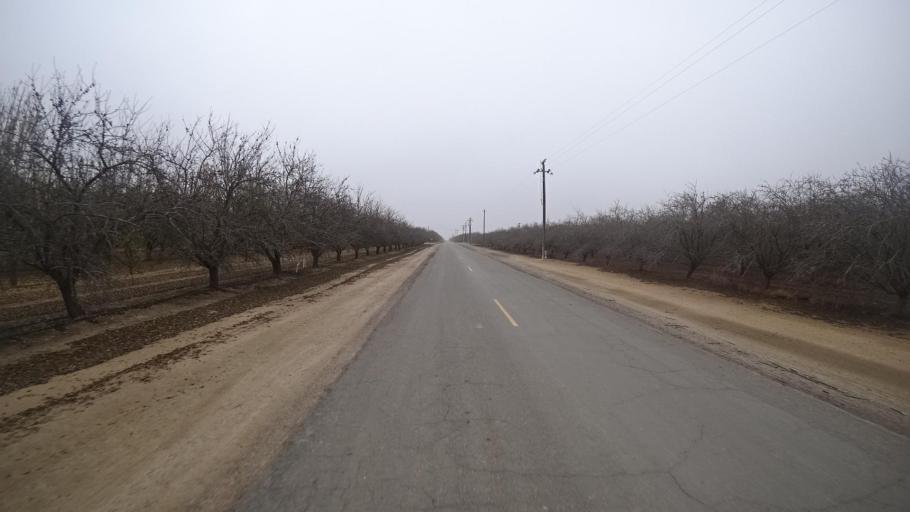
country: US
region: California
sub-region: Kern County
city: Wasco
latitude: 35.5882
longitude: -119.5093
